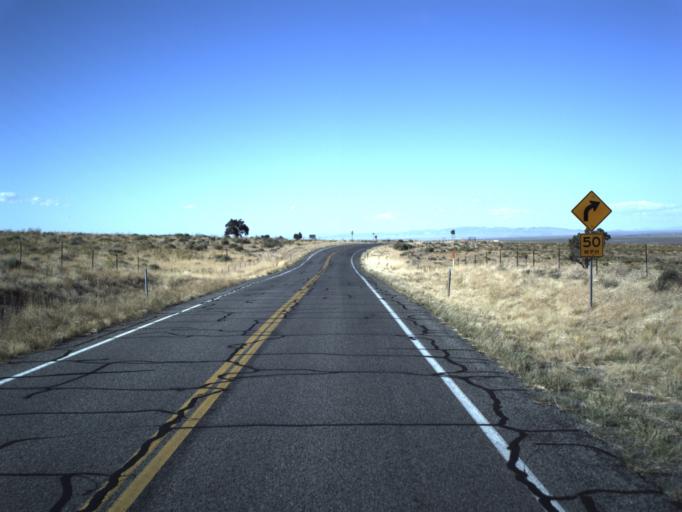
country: US
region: Utah
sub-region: Millard County
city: Delta
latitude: 39.3570
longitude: -112.3607
